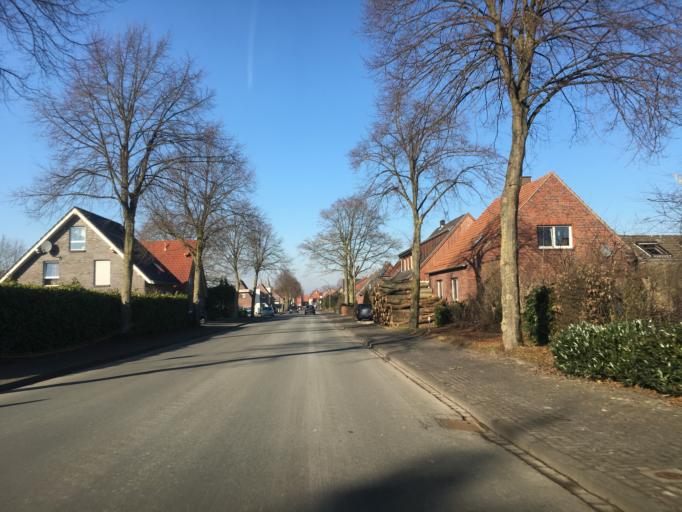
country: DE
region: North Rhine-Westphalia
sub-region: Regierungsbezirk Munster
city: Billerbeck
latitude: 52.0205
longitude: 7.2751
